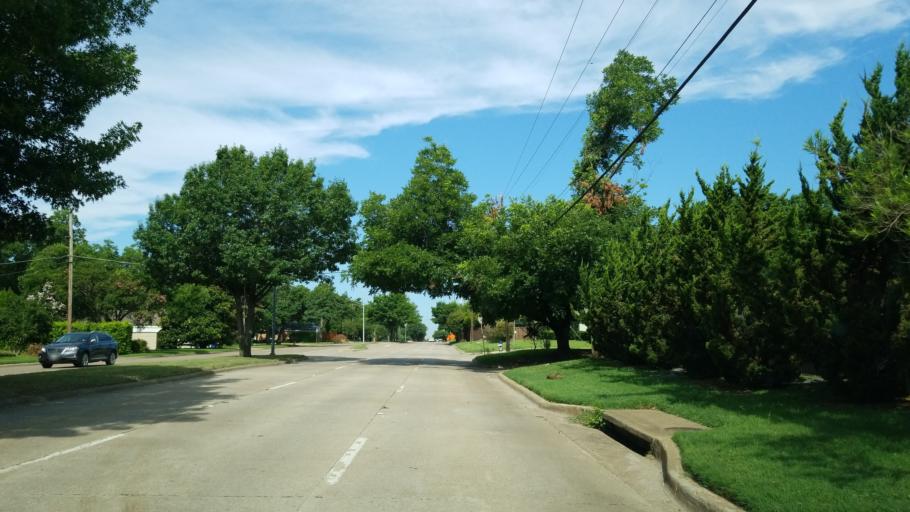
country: US
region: Texas
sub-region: Dallas County
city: University Park
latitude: 32.8951
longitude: -96.8419
